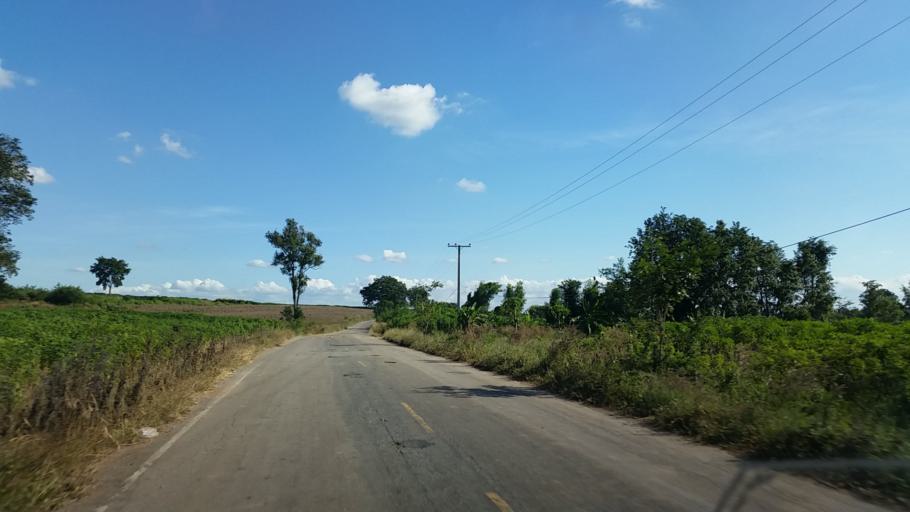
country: TH
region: Chaiyaphum
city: Thep Sathit
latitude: 15.5540
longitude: 101.4478
